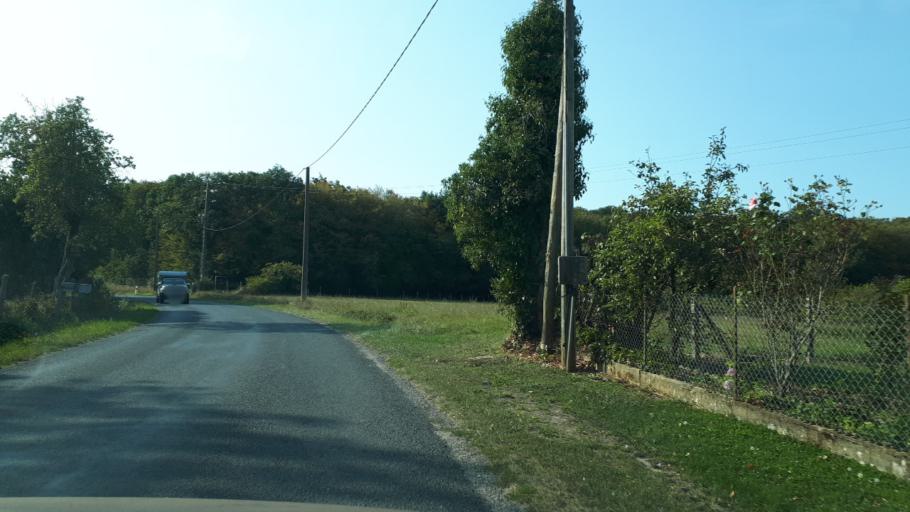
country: FR
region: Centre
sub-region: Departement du Cher
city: Menetou-Salon
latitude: 47.2313
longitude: 2.5031
